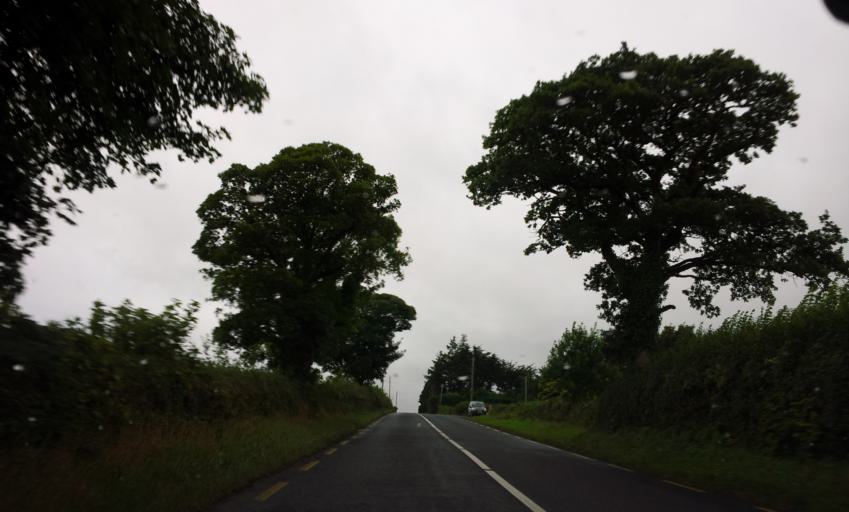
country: IE
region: Munster
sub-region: County Cork
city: Mitchelstown
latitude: 52.2504
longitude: -8.3895
